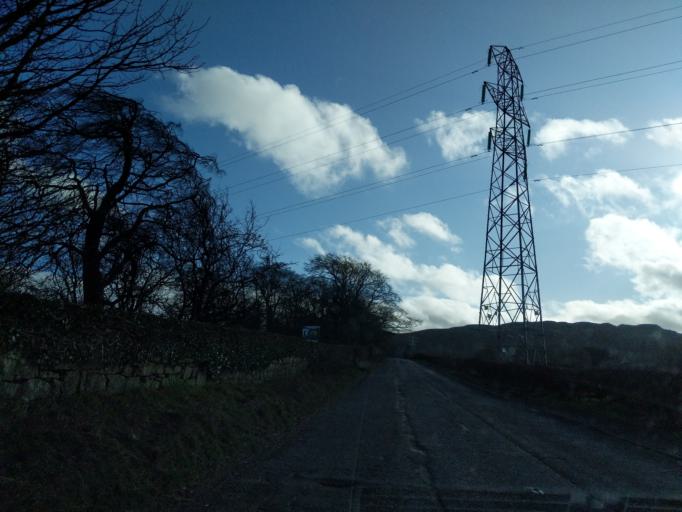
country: GB
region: Scotland
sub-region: Edinburgh
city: Ratho
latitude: 55.8971
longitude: -3.3845
